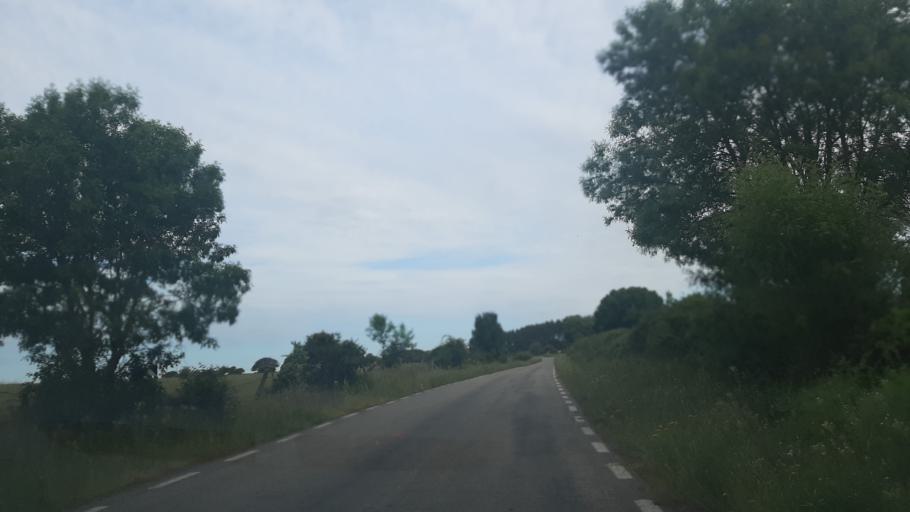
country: ES
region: Castille and Leon
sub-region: Provincia de Salamanca
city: Gallegos de Arganan
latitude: 40.6395
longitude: -6.7295
